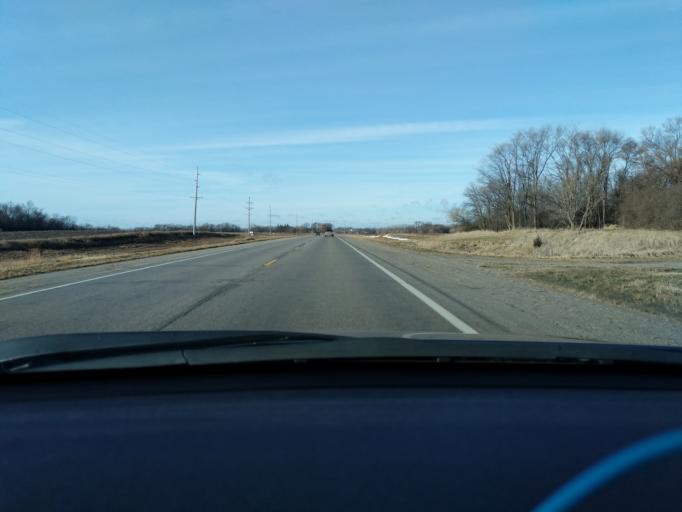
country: US
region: Minnesota
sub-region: Yellow Medicine County
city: Granite Falls
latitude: 44.7889
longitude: -95.4388
